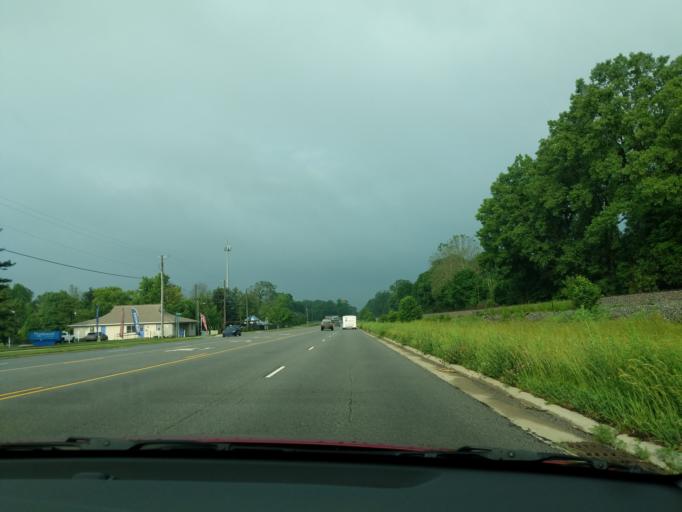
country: US
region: Indiana
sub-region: Hancock County
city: McCordsville
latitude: 39.8835
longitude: -85.9449
